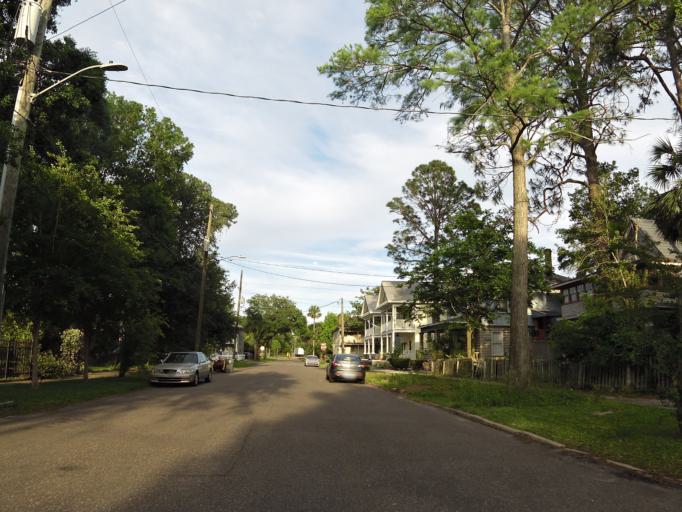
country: US
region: Florida
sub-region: Duval County
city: Jacksonville
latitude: 30.3426
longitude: -81.6474
